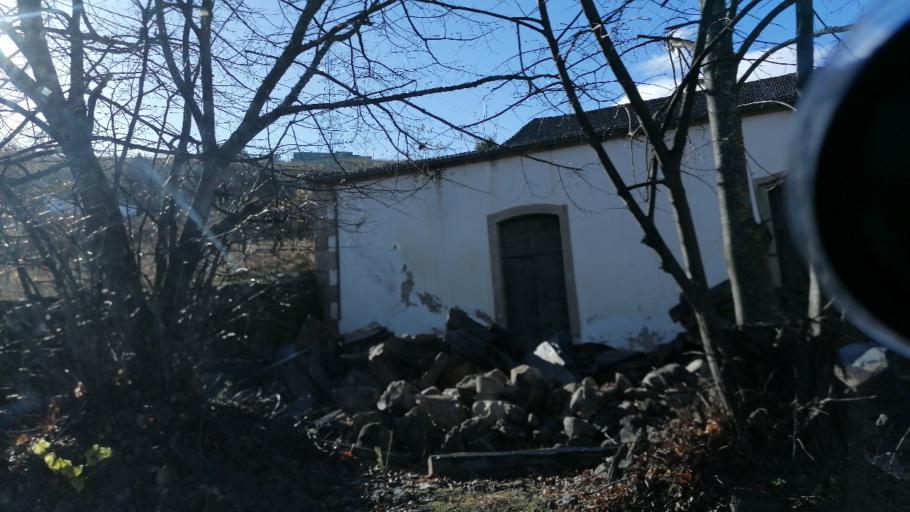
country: PT
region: Viseu
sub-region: Lamego
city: Lamego
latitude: 41.1192
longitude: -7.7957
